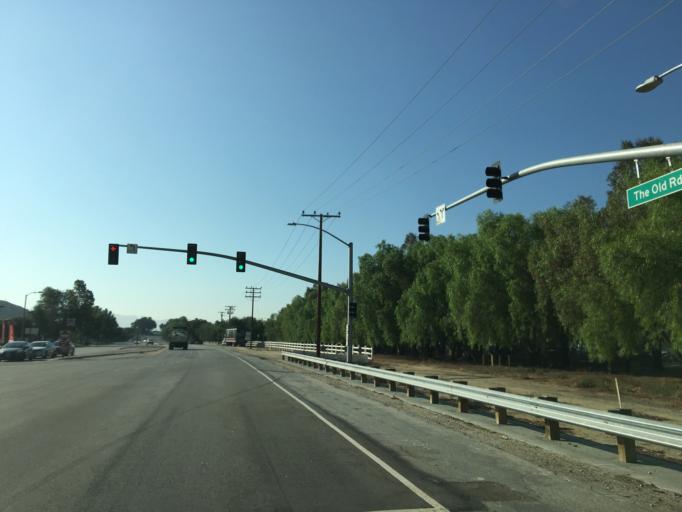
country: US
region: California
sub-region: Los Angeles County
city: Valencia
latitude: 34.4329
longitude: -118.5925
